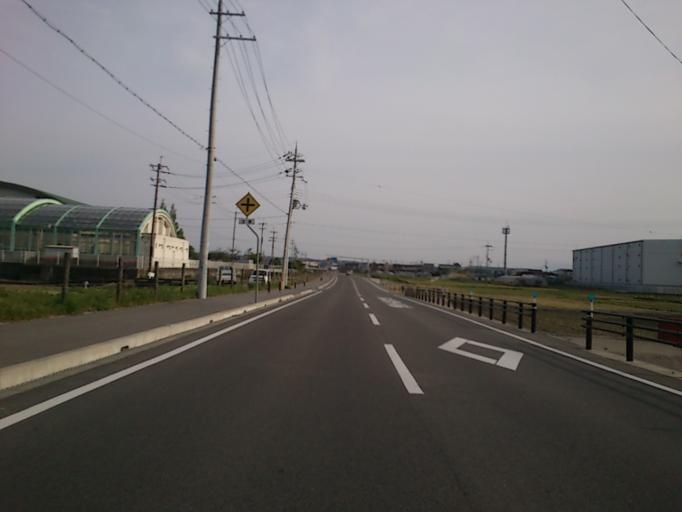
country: JP
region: Nara
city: Nara-shi
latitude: 34.7580
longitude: 135.8150
